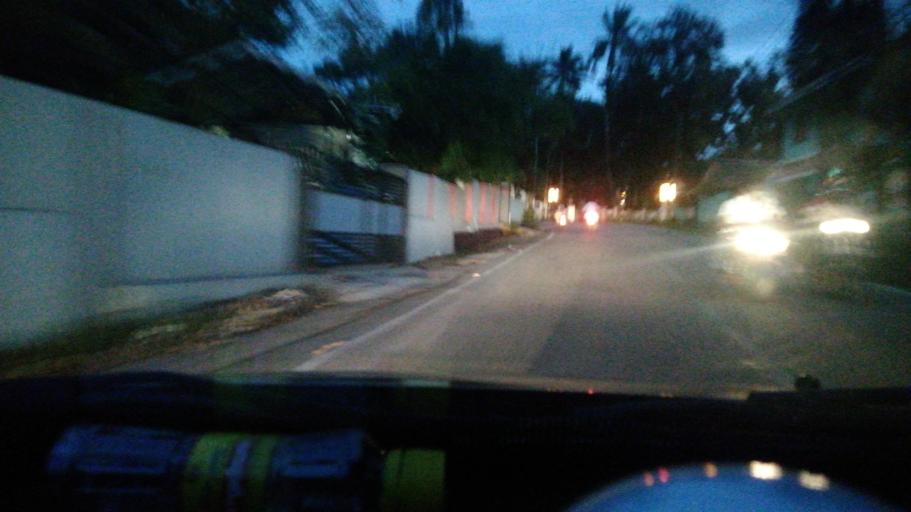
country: IN
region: Kerala
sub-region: Thiruvananthapuram
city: Paravur
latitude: 8.8128
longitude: 76.6764
